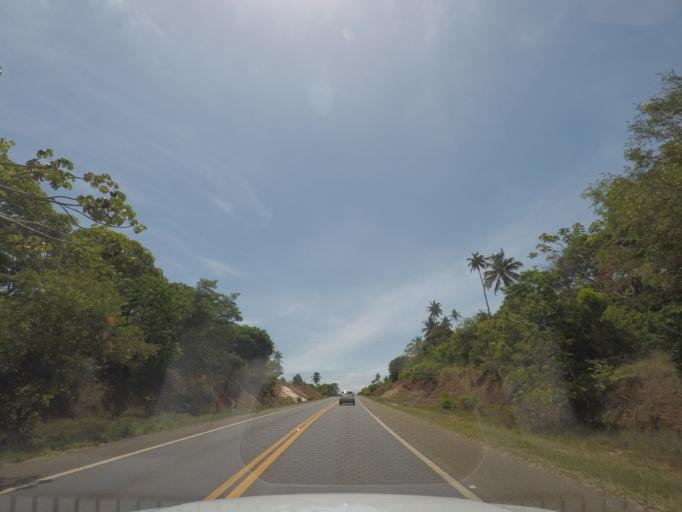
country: BR
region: Bahia
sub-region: Mata De Sao Joao
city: Mata de Sao Joao
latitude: -12.4344
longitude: -37.9446
